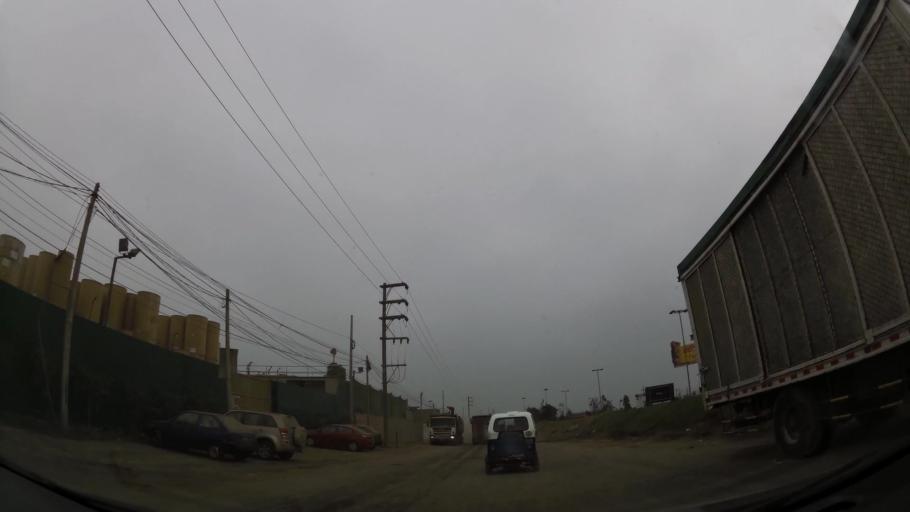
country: PE
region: Lima
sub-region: Lima
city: Surco
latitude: -12.2155
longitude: -76.9763
